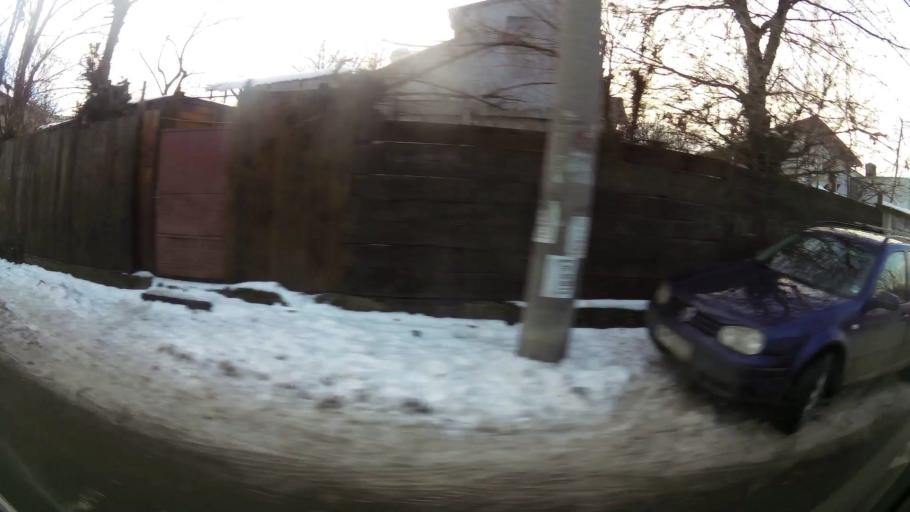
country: RO
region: Bucuresti
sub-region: Municipiul Bucuresti
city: Bucuresti
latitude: 44.3868
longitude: 26.0814
